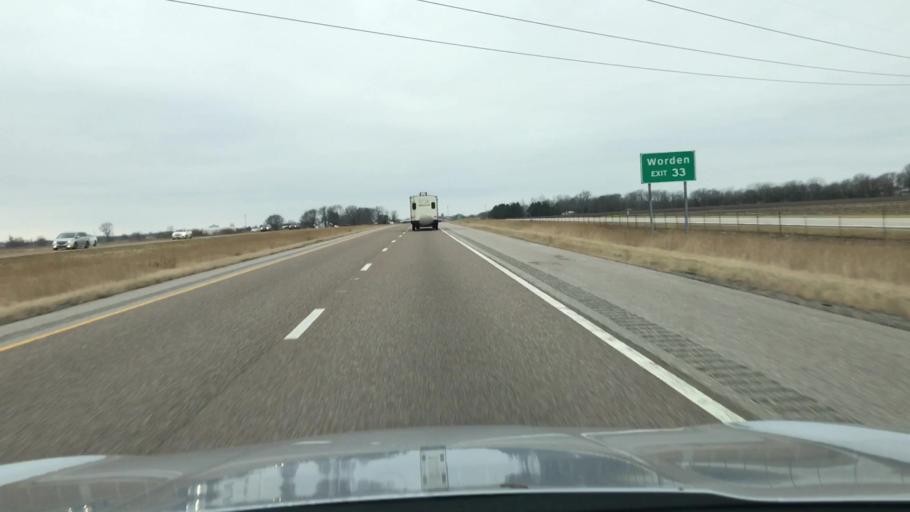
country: US
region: Illinois
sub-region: Madison County
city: Worden
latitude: 38.9435
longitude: -89.7856
